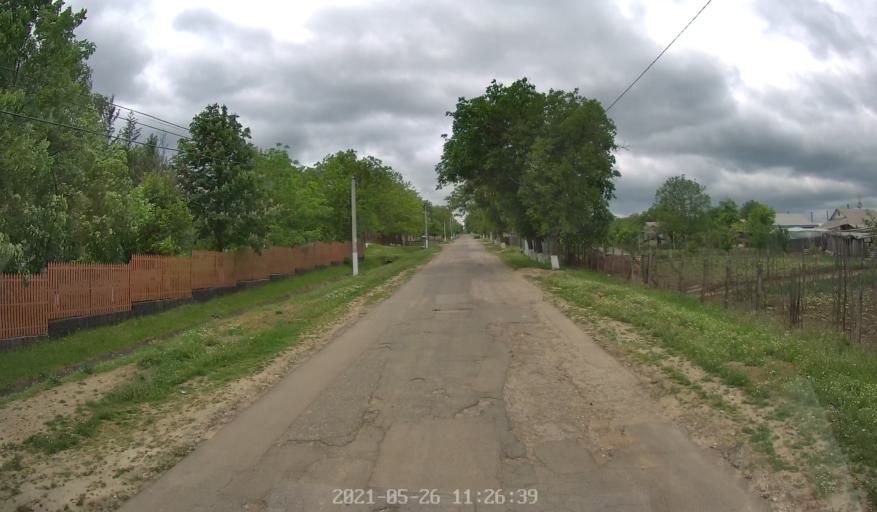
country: MD
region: Hincesti
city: Dancu
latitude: 46.8265
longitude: 28.3639
